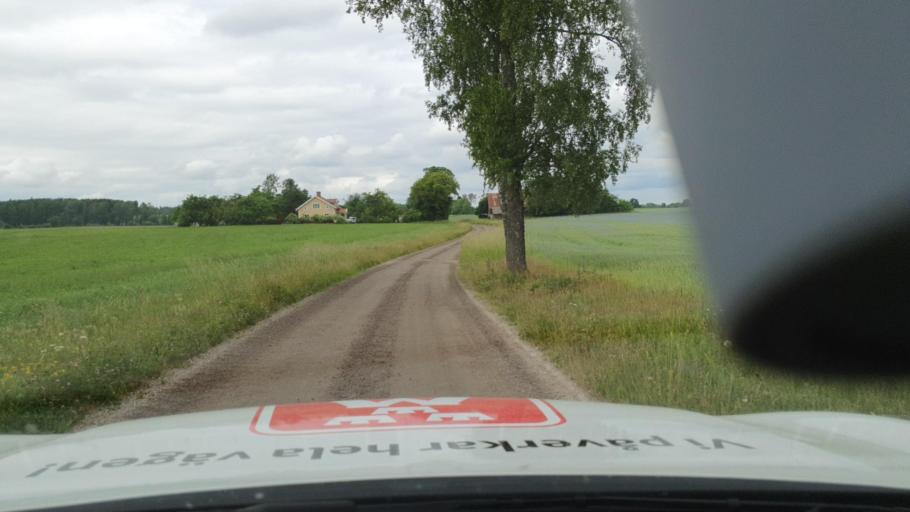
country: SE
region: Vaestra Goetaland
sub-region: Hjo Kommun
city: Hjo
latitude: 58.1869
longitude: 14.1759
